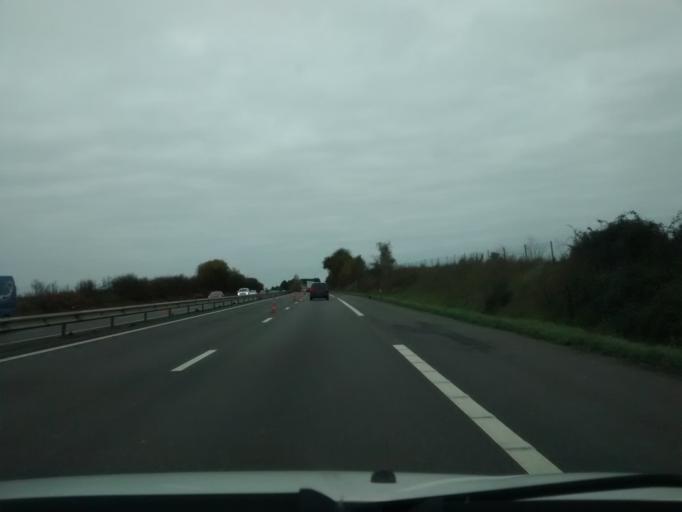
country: FR
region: Brittany
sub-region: Departement d'Ille-et-Vilaine
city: Saint-Didier
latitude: 48.0861
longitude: -1.3485
